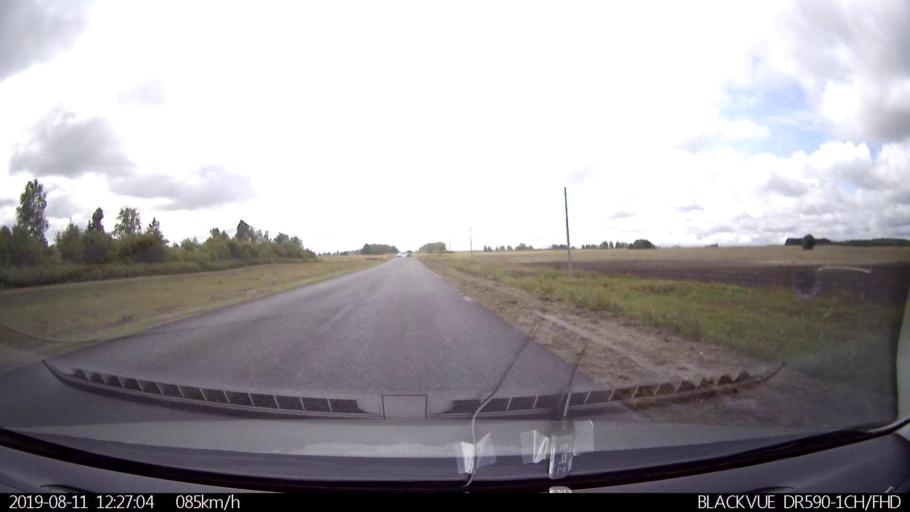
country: RU
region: Ulyanovsk
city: Ignatovka
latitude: 53.8581
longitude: 47.9249
